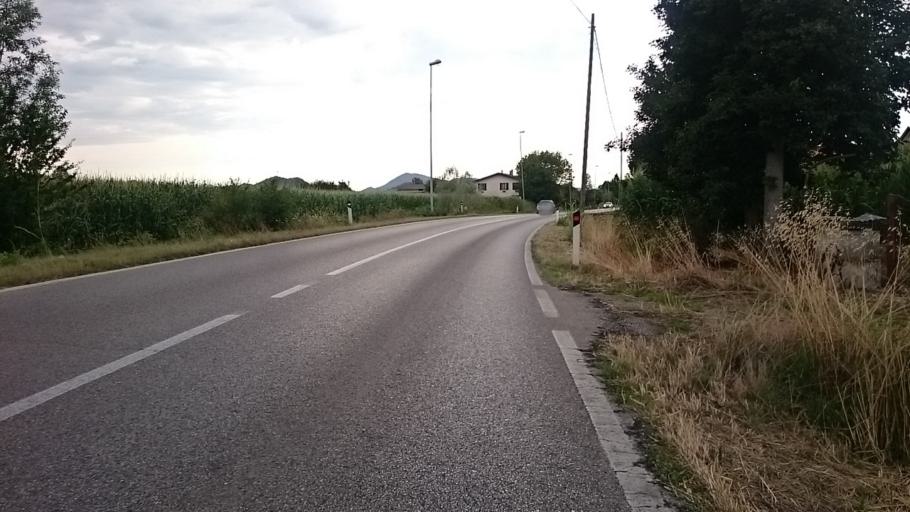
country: IT
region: Veneto
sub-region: Provincia di Padova
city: Terradura
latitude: 45.3217
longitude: 11.8419
